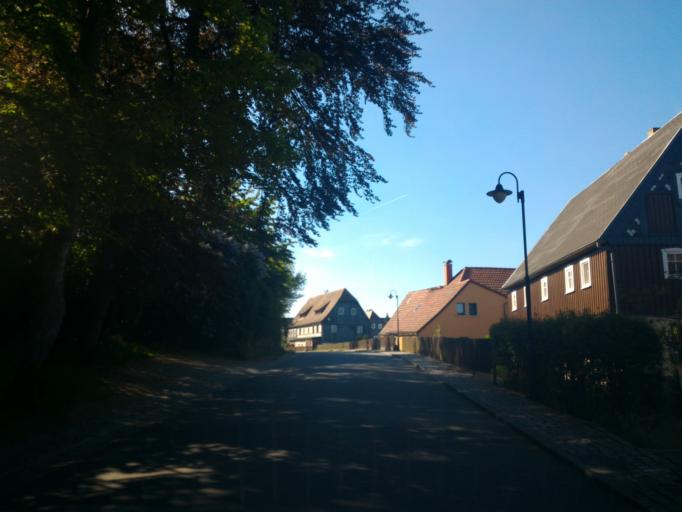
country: DE
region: Saxony
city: Niedercunnersdorf
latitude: 51.0398
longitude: 14.6655
